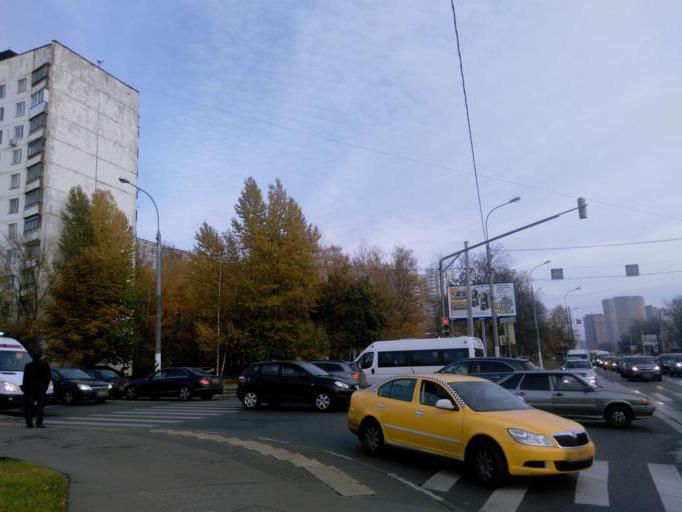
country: RU
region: Moscow
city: Troparevo
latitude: 55.6483
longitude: 37.5131
